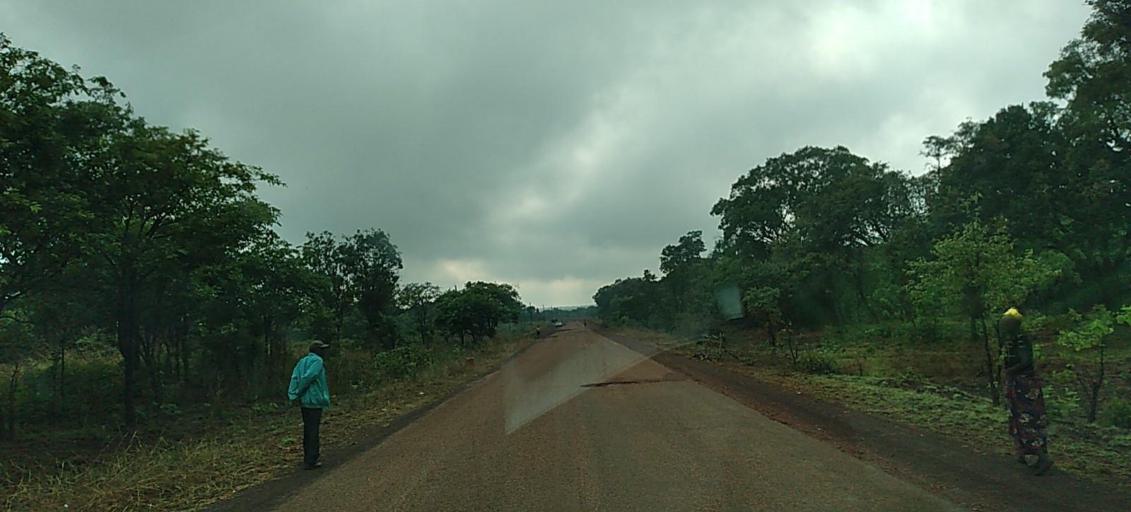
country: ZM
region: North-Western
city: Mwinilunga
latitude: -11.7250
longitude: 24.5698
